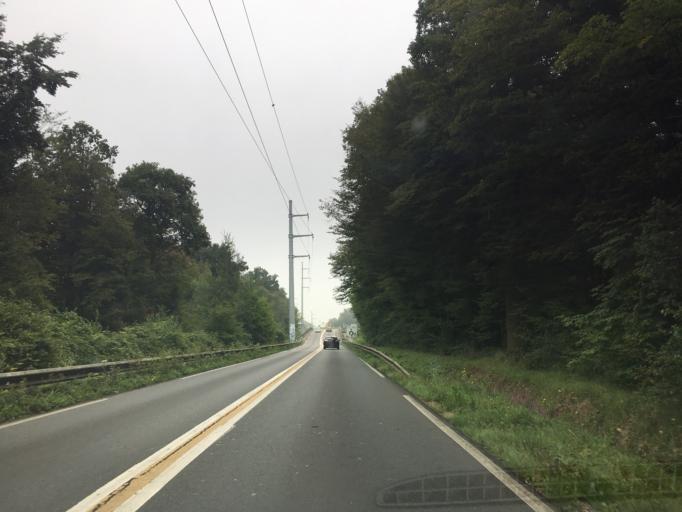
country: FR
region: Ile-de-France
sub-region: Departement de l'Essonne
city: Tigery
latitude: 48.6584
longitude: 2.5144
